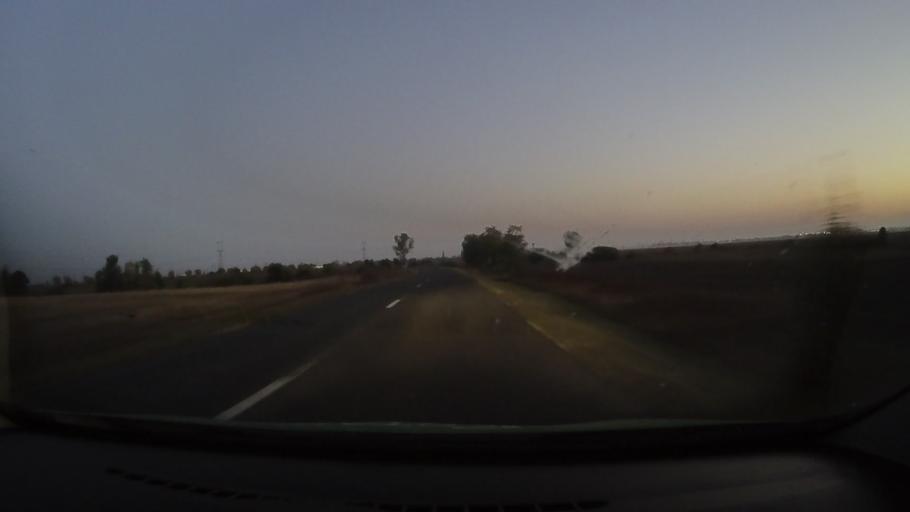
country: RO
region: Arad
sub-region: Comuna Livada
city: Livada
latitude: 46.2013
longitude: 21.3872
